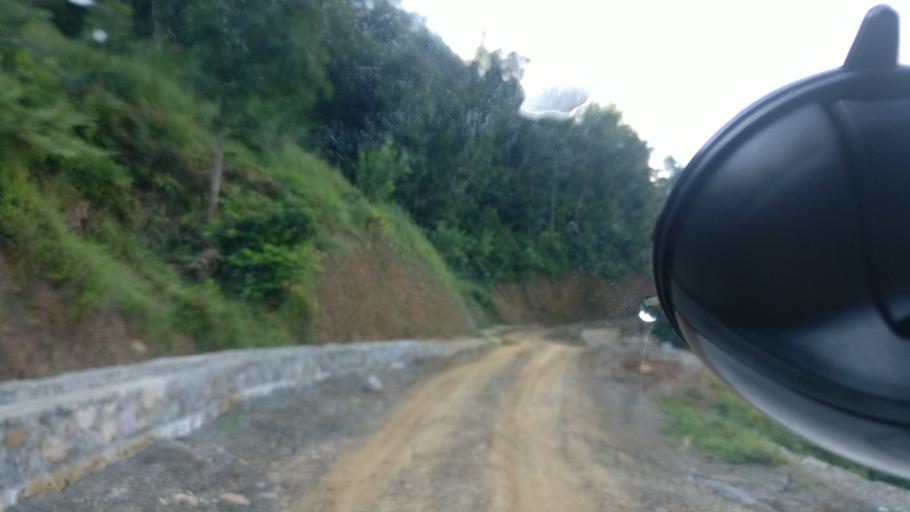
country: NP
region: Western Region
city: Baglung
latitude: 28.1518
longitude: 83.6559
